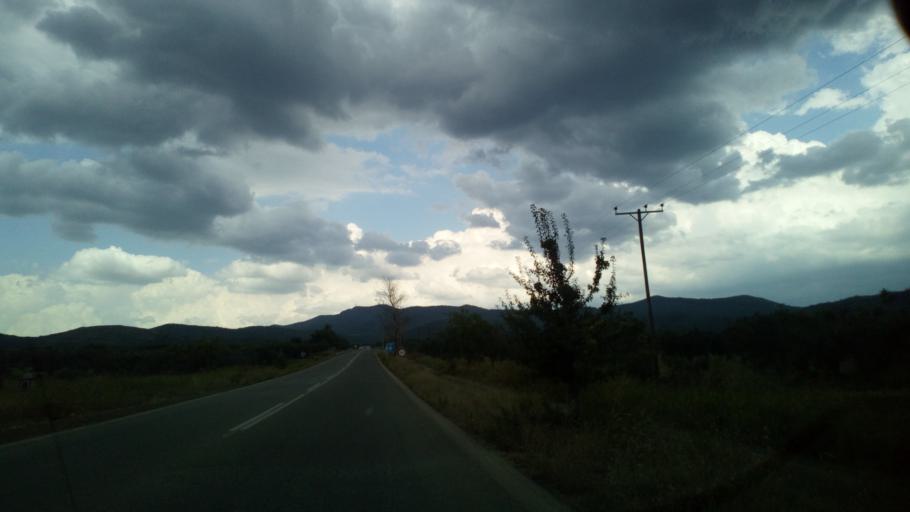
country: GR
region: Central Macedonia
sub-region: Nomos Chalkidikis
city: Polygyros
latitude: 40.3281
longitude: 23.4507
